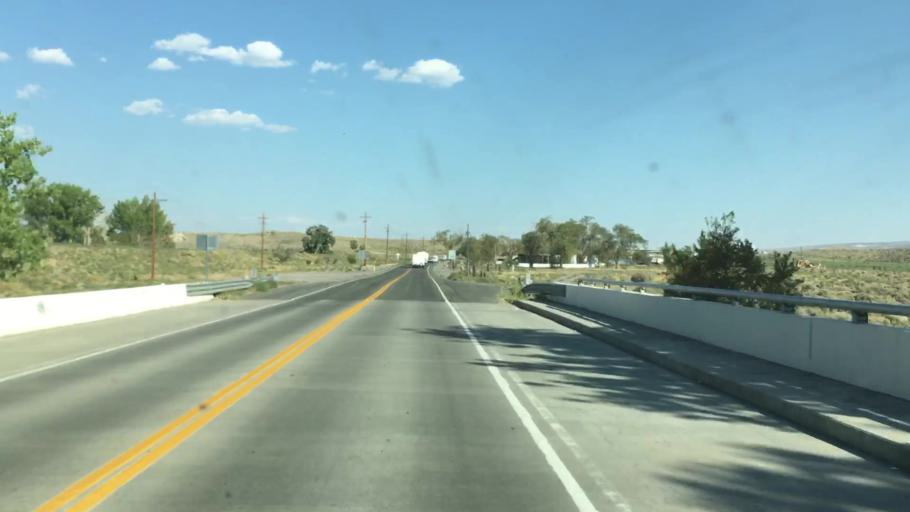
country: US
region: Nevada
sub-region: Lyon County
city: Fernley
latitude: 39.6319
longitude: -119.2828
